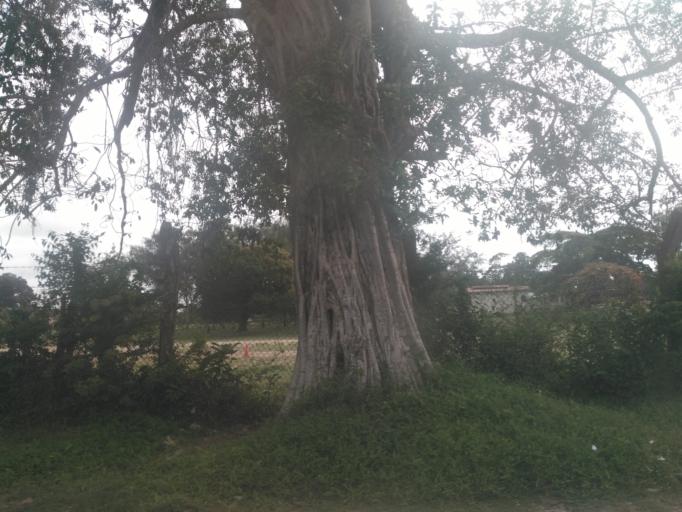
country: TZ
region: Zanzibar Urban/West
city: Zanzibar
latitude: -6.1739
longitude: 39.2037
